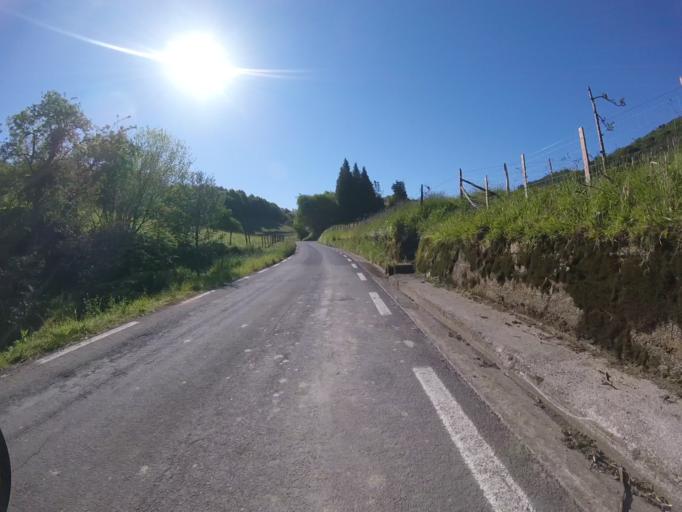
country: ES
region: Basque Country
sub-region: Provincia de Guipuzcoa
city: Aizarnazabal
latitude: 43.2314
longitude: -2.2199
